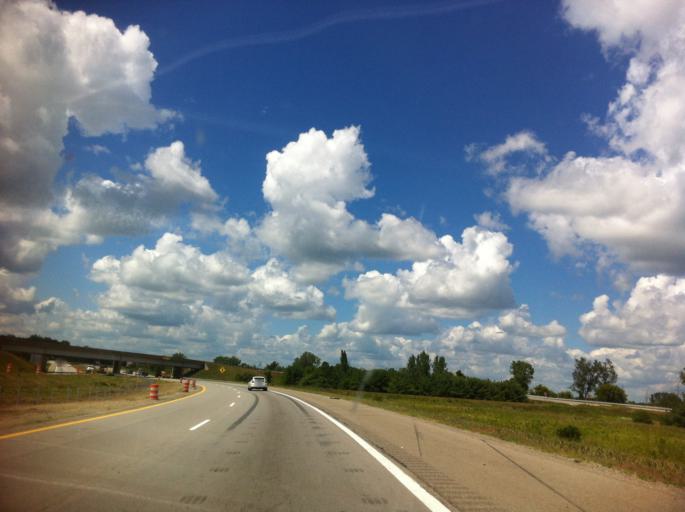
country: US
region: Michigan
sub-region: Washtenaw County
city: Milan
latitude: 42.0987
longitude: -83.6748
